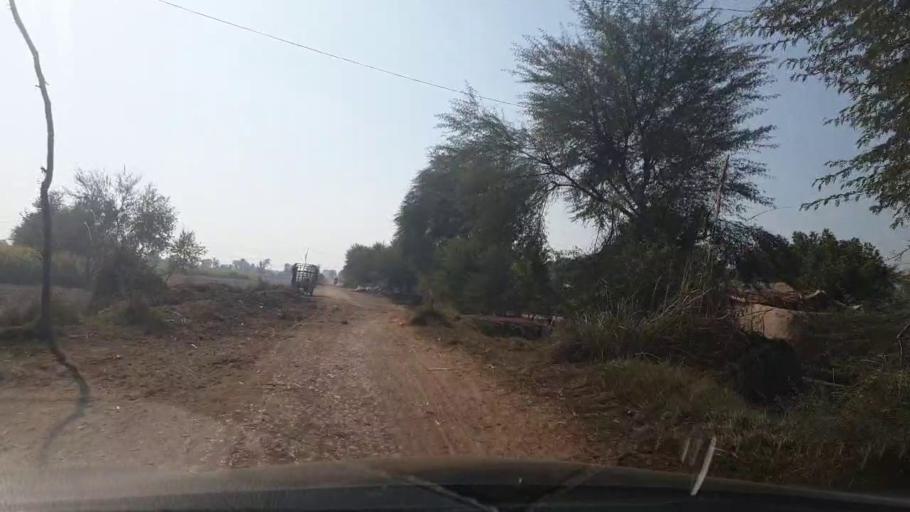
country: PK
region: Sindh
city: Ubauro
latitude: 28.1520
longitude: 69.6934
